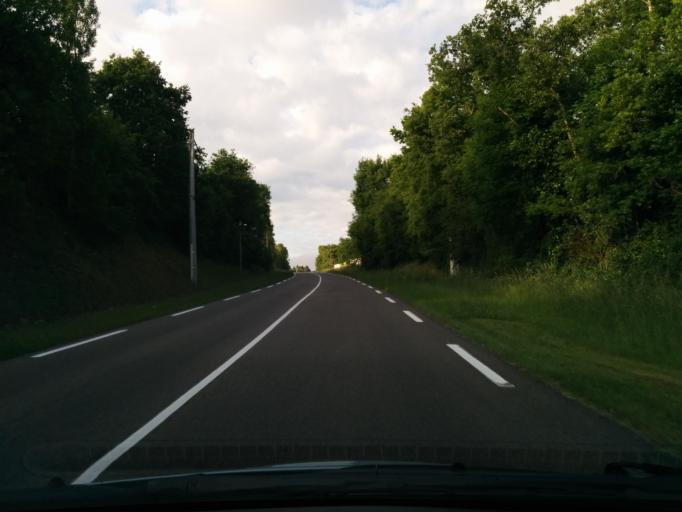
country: FR
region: Ile-de-France
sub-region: Departement des Yvelines
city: Follainville-Dennemont
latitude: 49.0483
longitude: 1.6914
